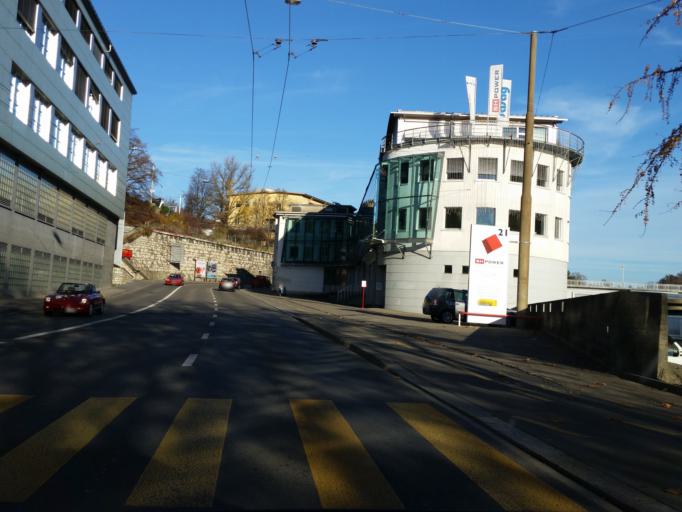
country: CH
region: Schaffhausen
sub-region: Bezirk Schaffhausen
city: Schaffhausen
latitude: 47.6932
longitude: 8.6286
